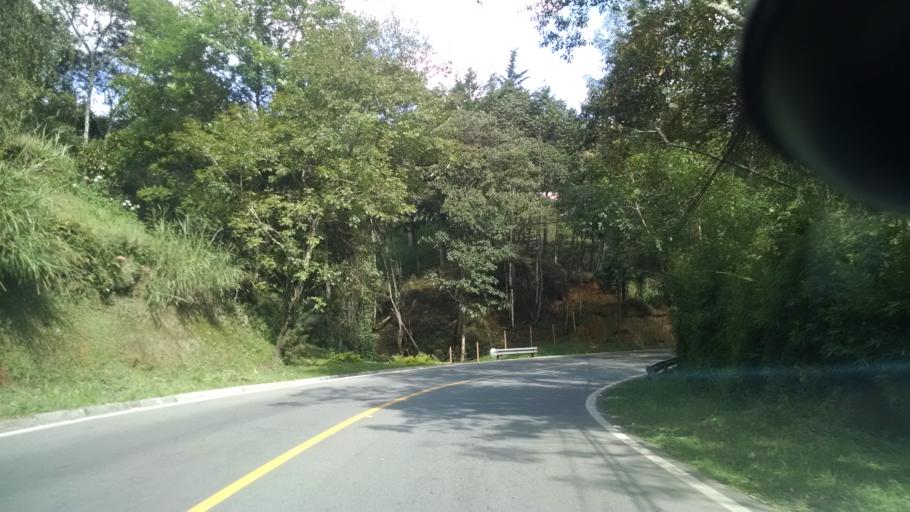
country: CO
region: Antioquia
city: El Retiro
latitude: 6.0857
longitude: -75.4781
